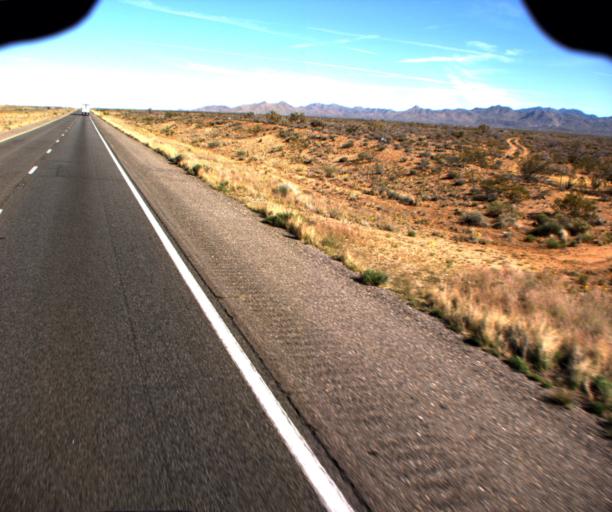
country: US
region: Arizona
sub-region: Mohave County
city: Golden Valley
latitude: 35.3416
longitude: -114.2191
